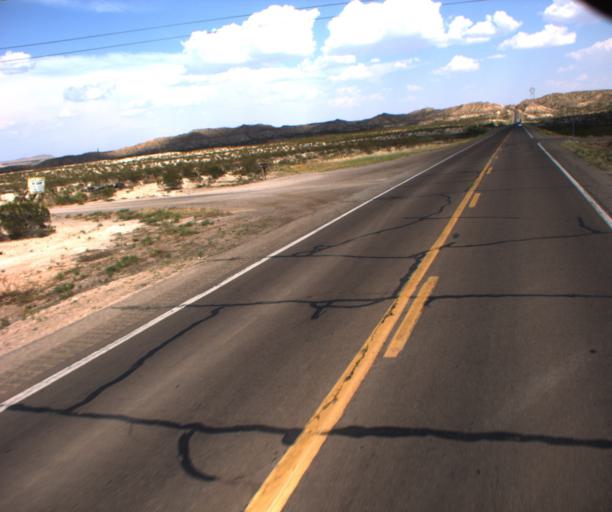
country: US
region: Arizona
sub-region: Greenlee County
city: Clifton
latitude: 32.7628
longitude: -109.1424
